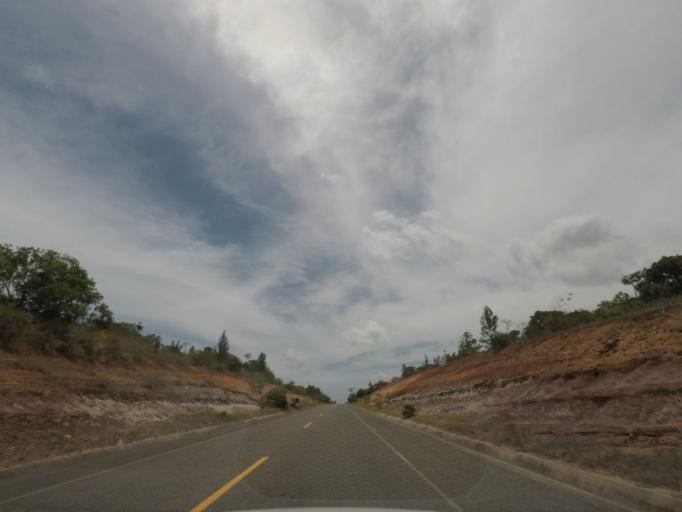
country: BR
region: Bahia
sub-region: Conde
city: Conde
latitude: -11.8971
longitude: -37.6521
